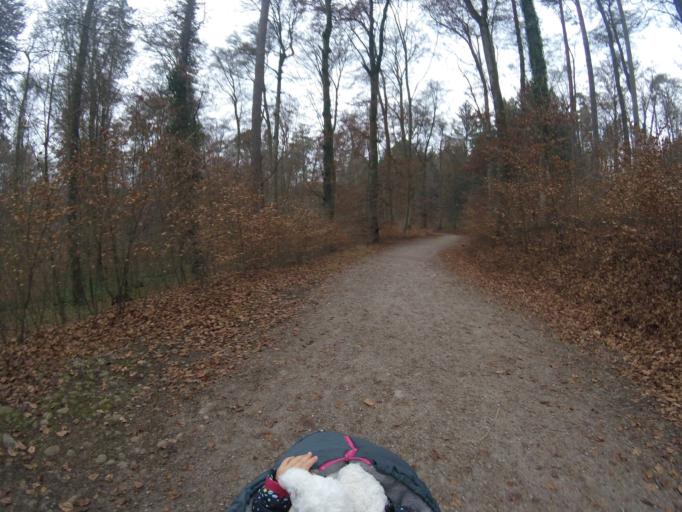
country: CH
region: Bern
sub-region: Bern-Mittelland District
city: Bern
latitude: 46.9358
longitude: 7.4567
